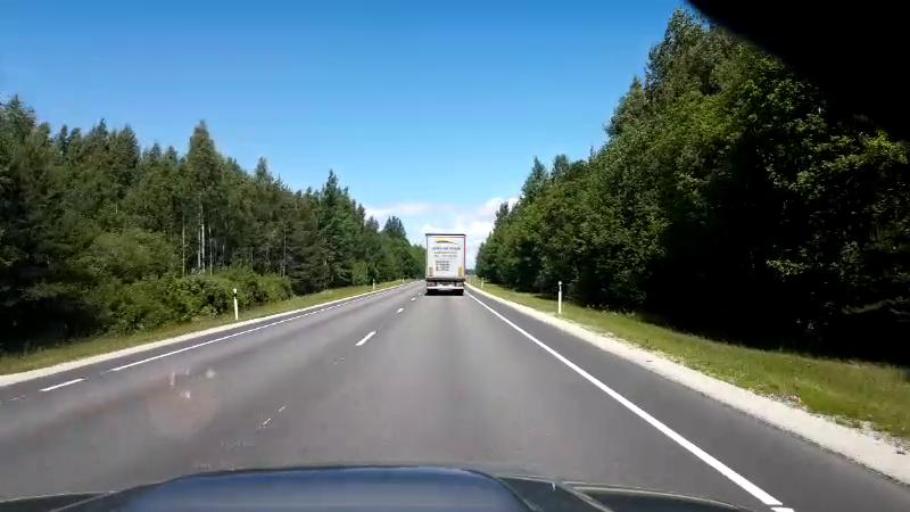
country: EE
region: Paernumaa
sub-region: Paernu linn
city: Parnu
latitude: 58.1055
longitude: 24.5085
